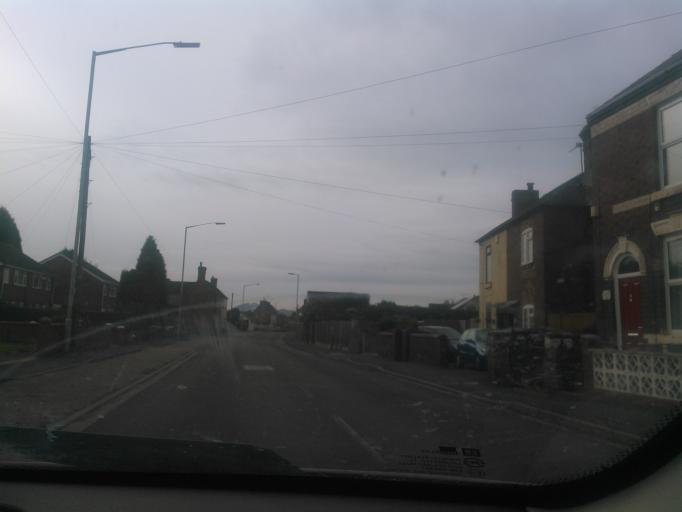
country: GB
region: England
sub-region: Telford and Wrekin
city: Oakengates
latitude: 52.7148
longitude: -2.4508
